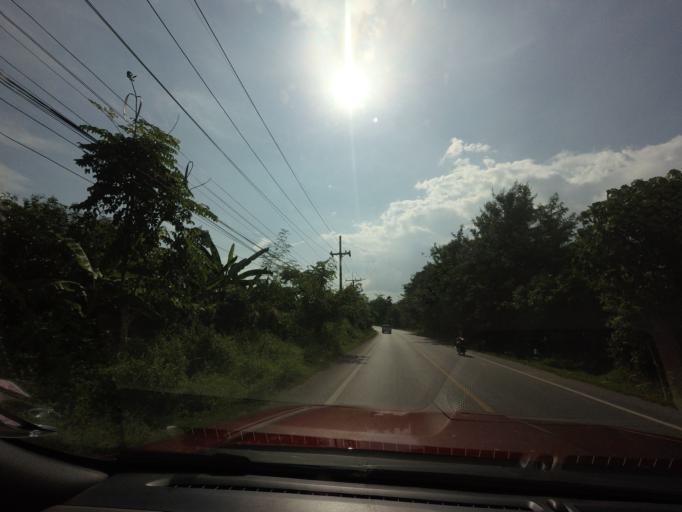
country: TH
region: Yala
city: Yala
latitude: 6.5498
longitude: 101.2385
